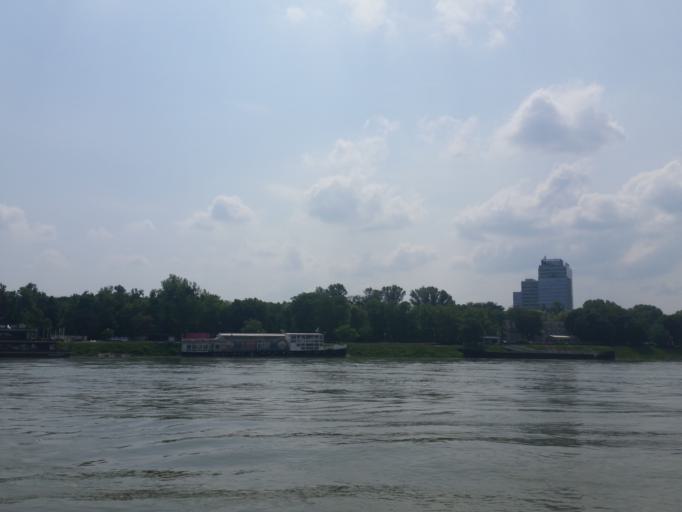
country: SK
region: Bratislavsky
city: Bratislava
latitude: 48.1392
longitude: 17.1126
